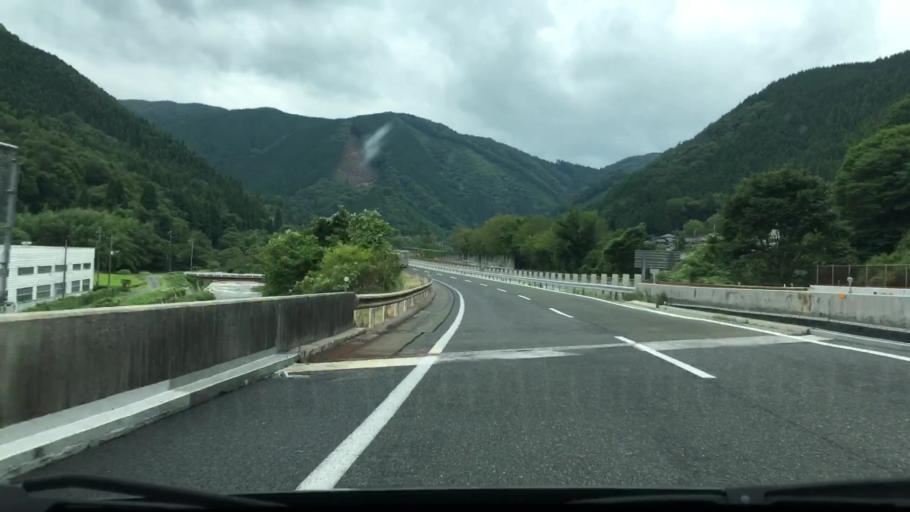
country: JP
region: Okayama
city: Niimi
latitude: 34.9788
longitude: 133.3734
